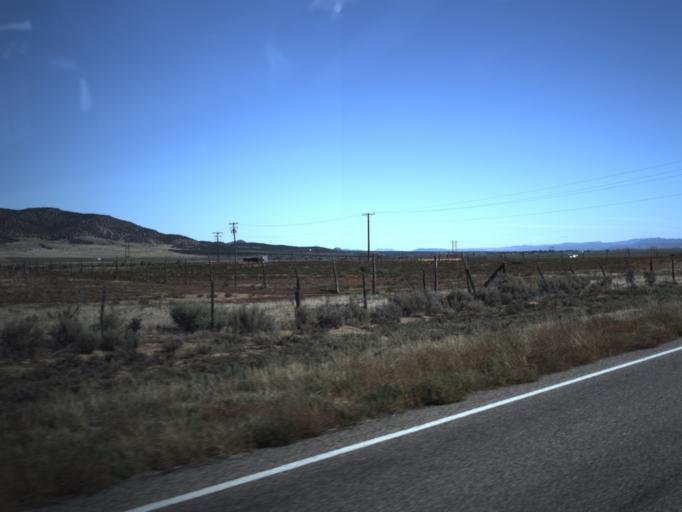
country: US
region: Utah
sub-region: Iron County
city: Cedar City
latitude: 37.6539
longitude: -113.2263
